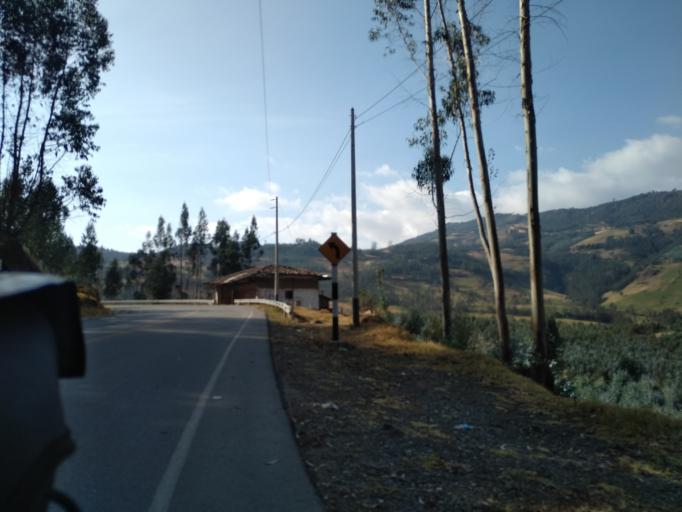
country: PE
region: La Libertad
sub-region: Provincia de Otuzco
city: Agallpampa
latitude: -7.9959
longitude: -78.5124
